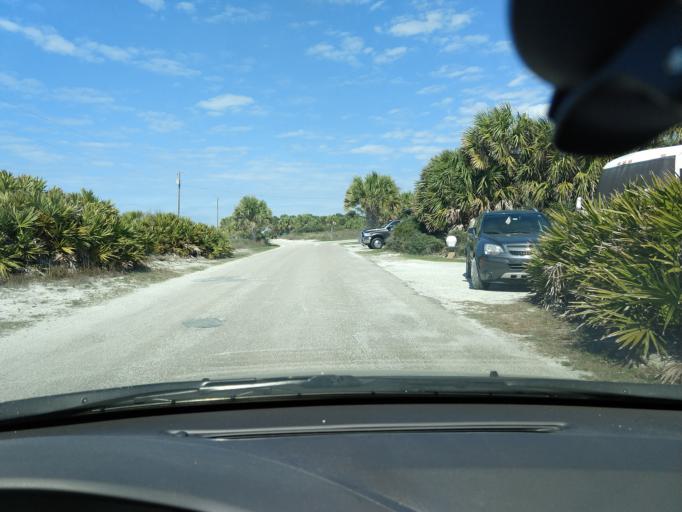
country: US
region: Florida
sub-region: Gulf County
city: Port Saint Joe
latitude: 29.7728
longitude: -85.4059
